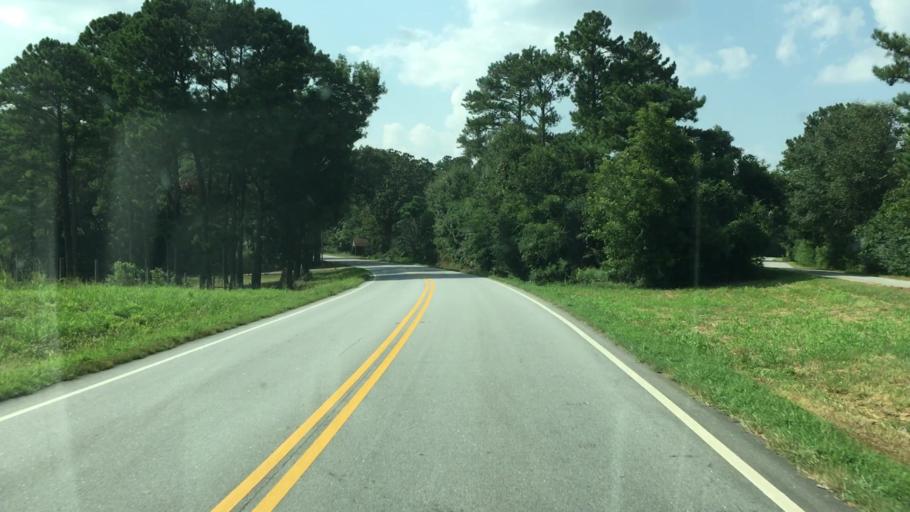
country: US
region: Georgia
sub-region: Jasper County
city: Monticello
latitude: 33.3521
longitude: -83.7225
